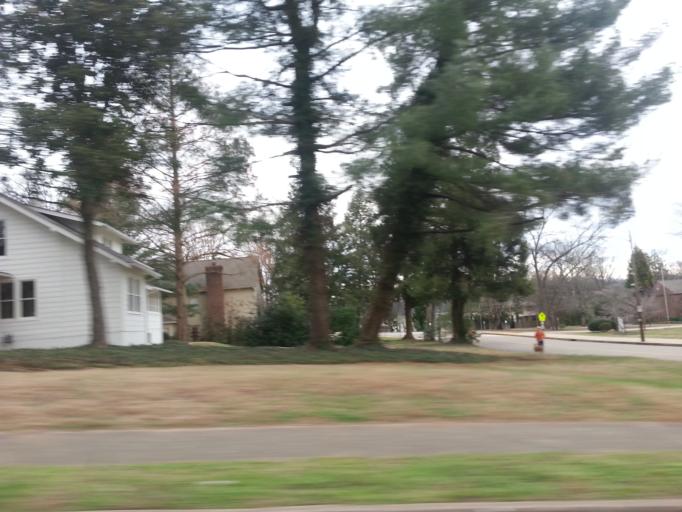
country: US
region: Tennessee
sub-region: Knox County
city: Knoxville
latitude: 35.9362
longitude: -83.9685
